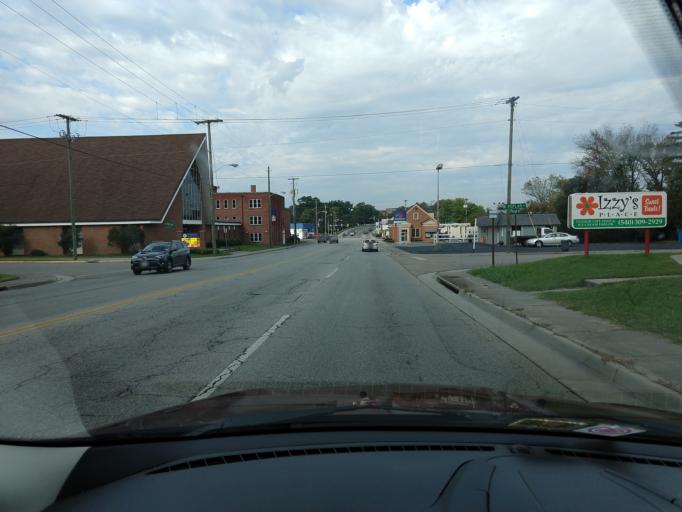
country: US
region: Virginia
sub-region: Roanoke County
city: Vinton
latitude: 37.2818
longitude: -79.8983
